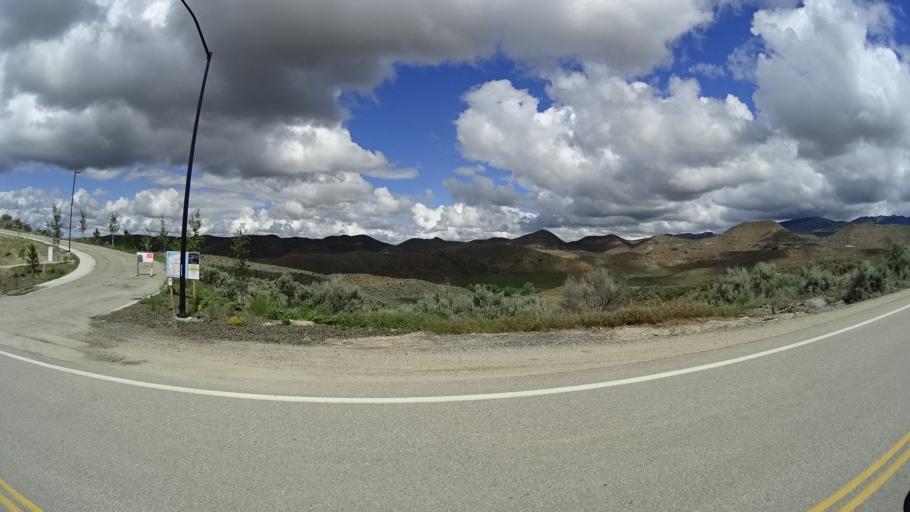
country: US
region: Idaho
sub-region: Ada County
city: Boise
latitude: 43.6646
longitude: -116.1915
